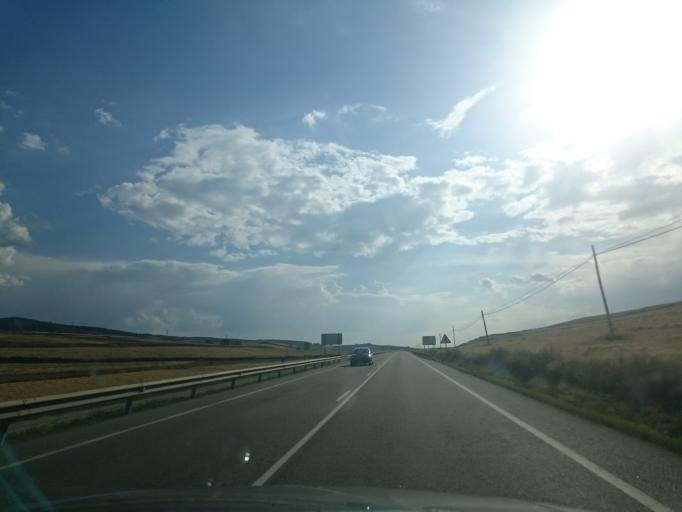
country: ES
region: Castille and Leon
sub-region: Provincia de Burgos
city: Fresnena
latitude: 42.4238
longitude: -3.1494
